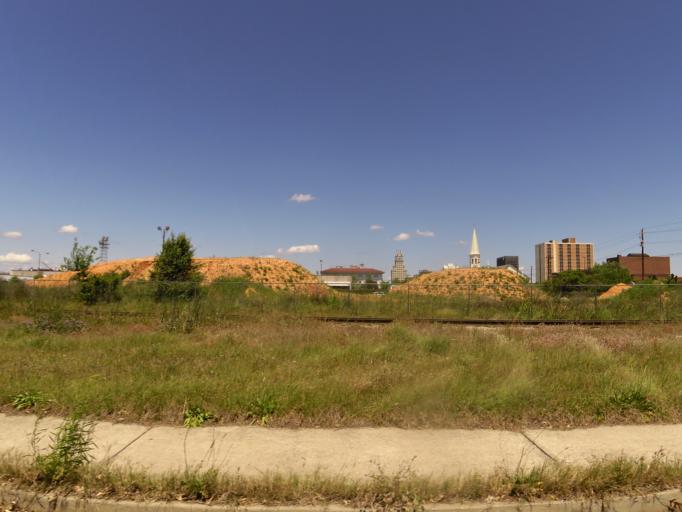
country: US
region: Georgia
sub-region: Richmond County
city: Augusta
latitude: 33.4695
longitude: -81.9688
